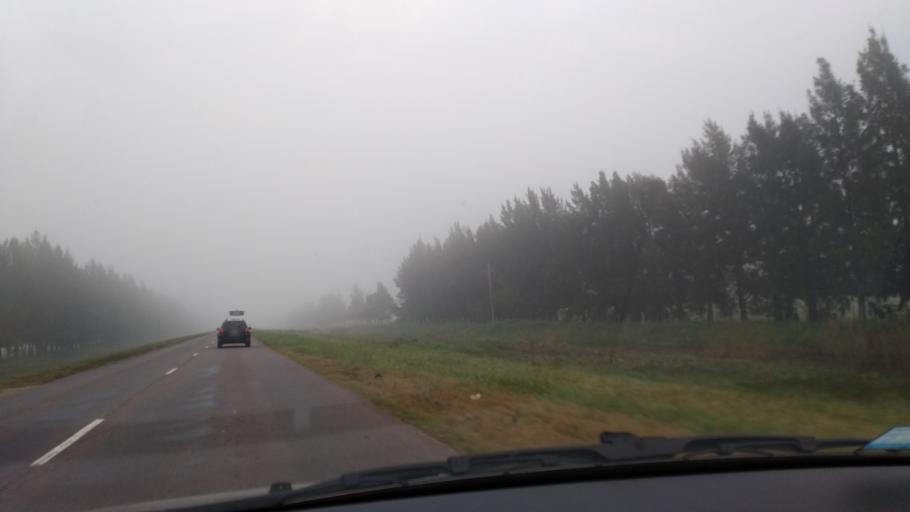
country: AR
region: Buenos Aires
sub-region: Partido de San Vicente
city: San Vicente
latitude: -35.2730
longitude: -58.5419
